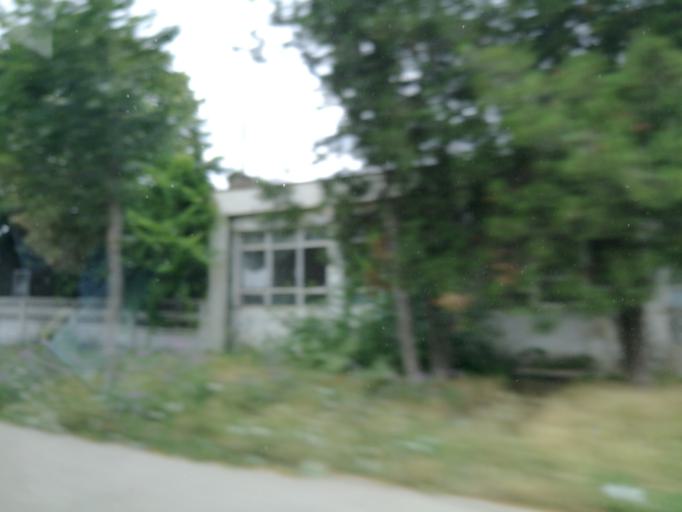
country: RO
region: Constanta
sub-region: Municipiul Mangalia
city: Mangalia
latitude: 43.8150
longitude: 28.5728
